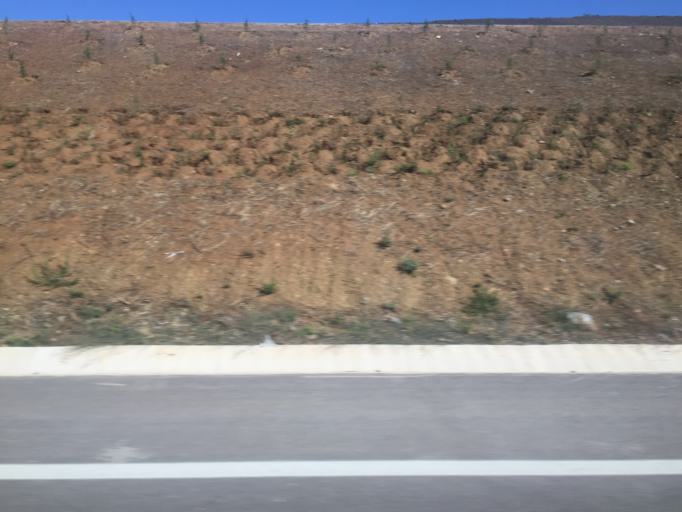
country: TR
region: Bursa
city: Mahmudiye
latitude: 40.2768
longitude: 28.5300
